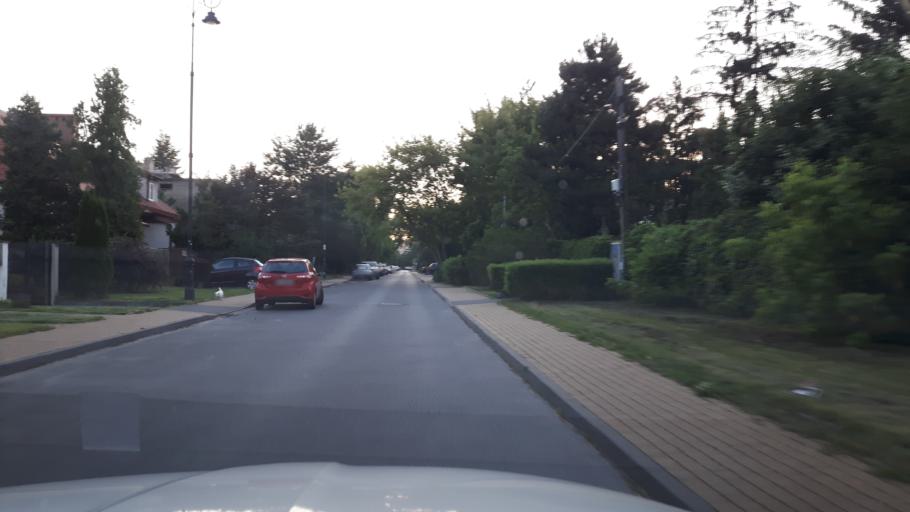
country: PL
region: Masovian Voivodeship
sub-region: Warszawa
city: Wilanow
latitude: 52.1906
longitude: 21.0699
